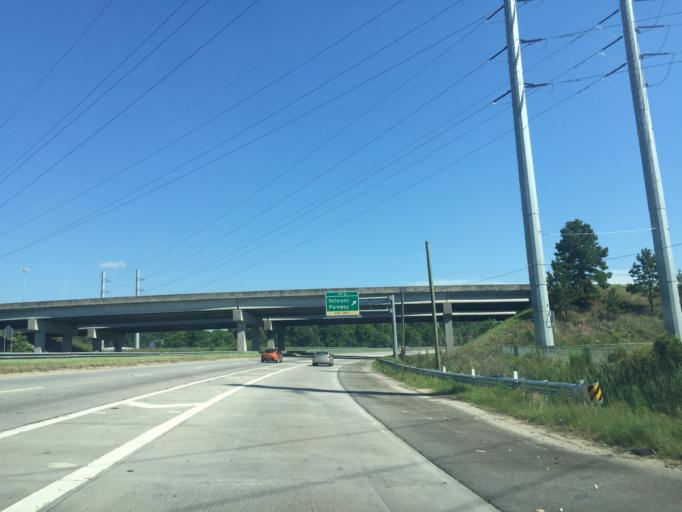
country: US
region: Georgia
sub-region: Chatham County
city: Savannah
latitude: 32.0410
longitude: -81.1457
